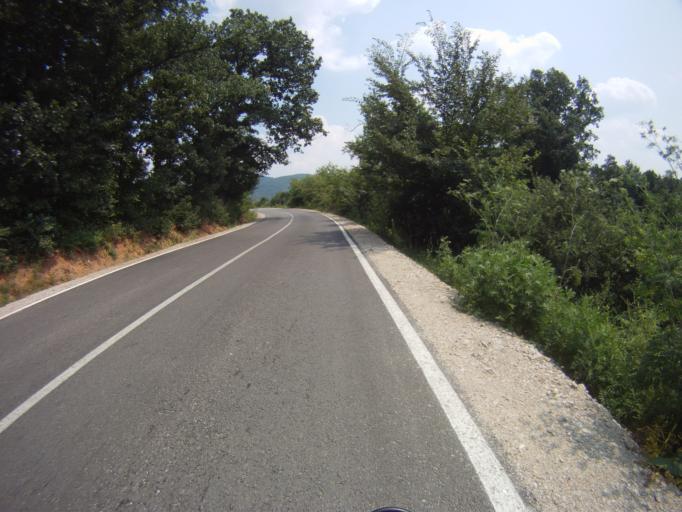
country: RS
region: Central Serbia
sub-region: Nisavski Okrug
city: Gadzin Han
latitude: 43.2076
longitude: 22.0150
